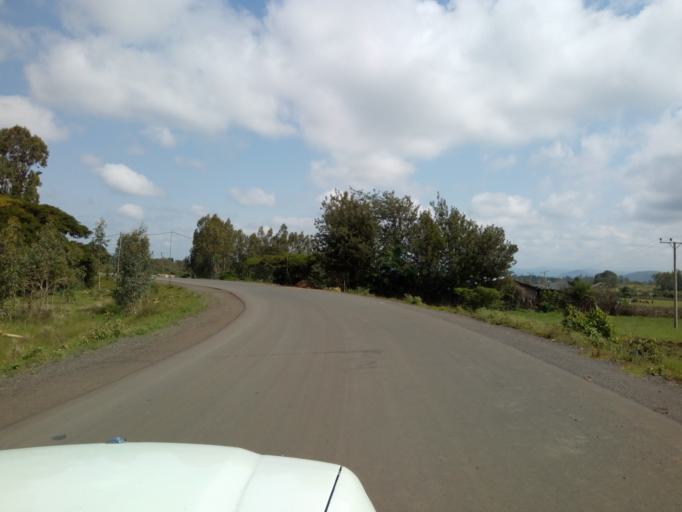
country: ET
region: Oromiya
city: Waliso
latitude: 8.5585
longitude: 37.9491
